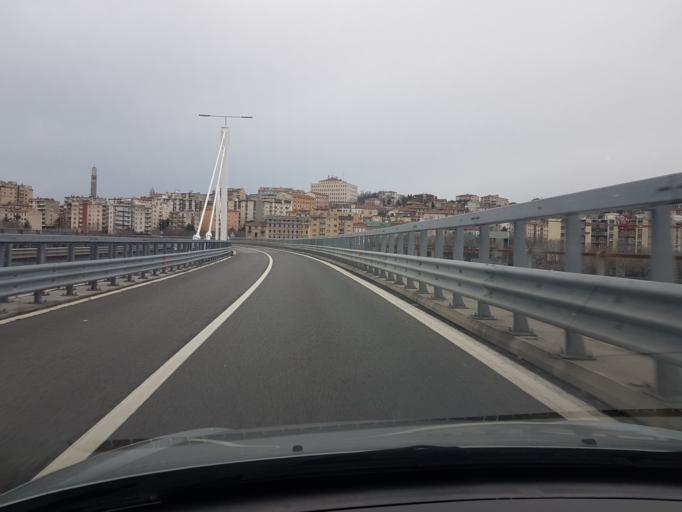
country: IT
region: Friuli Venezia Giulia
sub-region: Provincia di Trieste
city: Trieste
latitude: 45.6377
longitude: 13.7761
